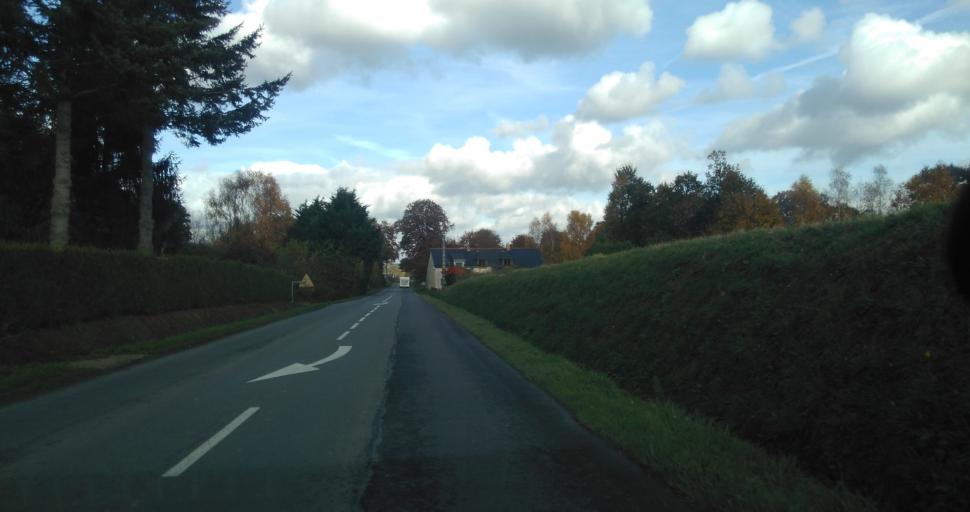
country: FR
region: Brittany
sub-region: Departement d'Ille-et-Vilaine
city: Boisgervilly
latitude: 48.1687
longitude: -2.0538
